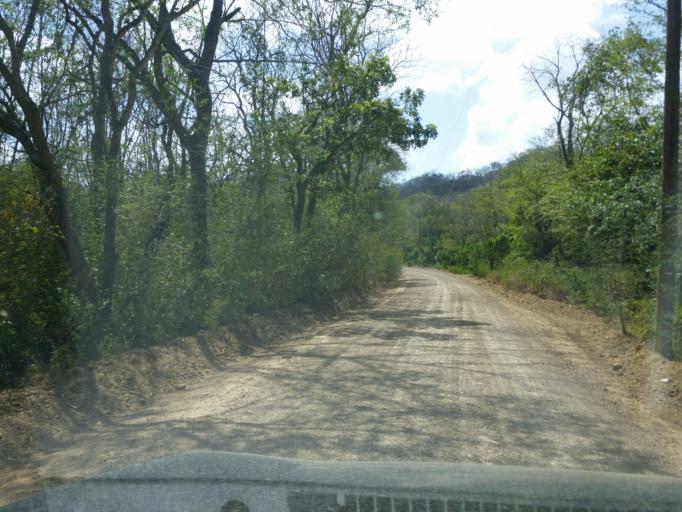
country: CR
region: Guanacaste
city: La Cruz
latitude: 11.1251
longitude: -85.7794
